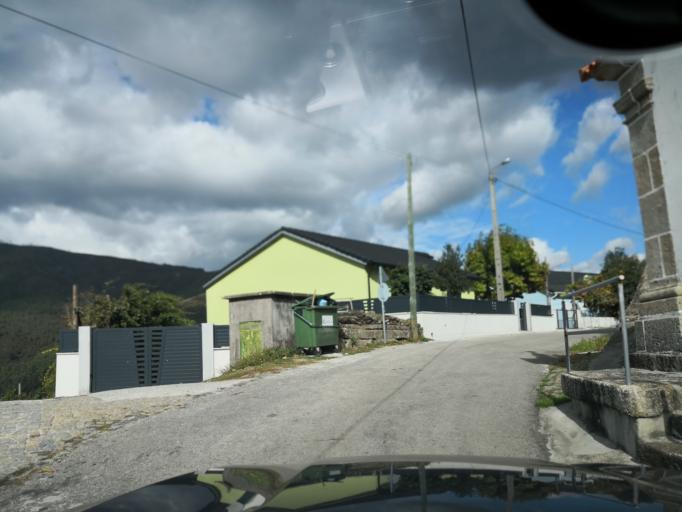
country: PT
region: Vila Real
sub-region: Mondim de Basto
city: Mondim de Basto
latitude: 41.3641
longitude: -7.8862
